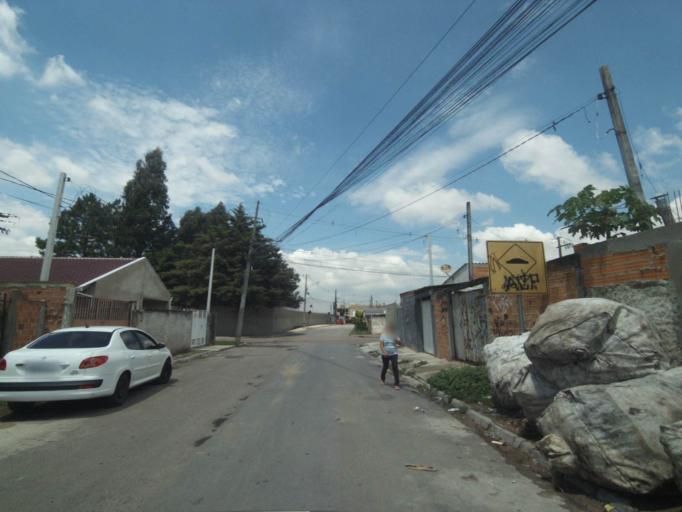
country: BR
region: Parana
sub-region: Pinhais
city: Pinhais
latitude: -25.4719
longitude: -49.1884
